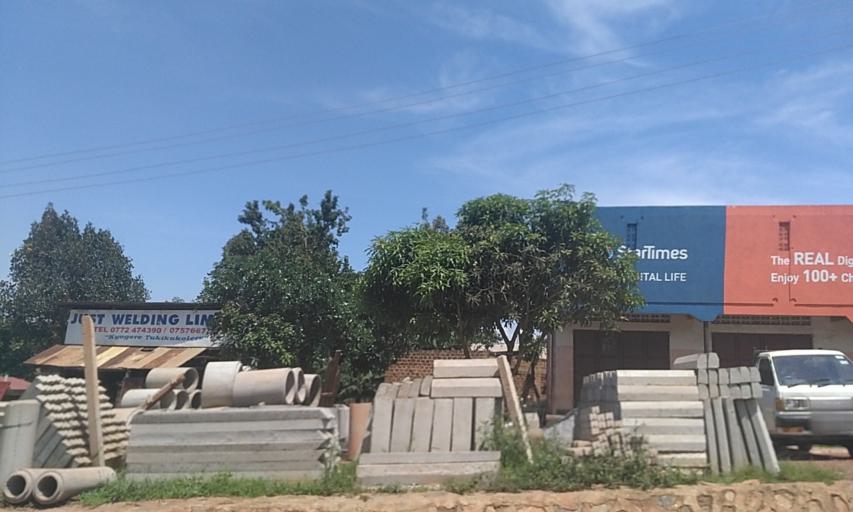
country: UG
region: Central Region
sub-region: Wakiso District
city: Wakiso
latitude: 0.4128
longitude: 32.4586
